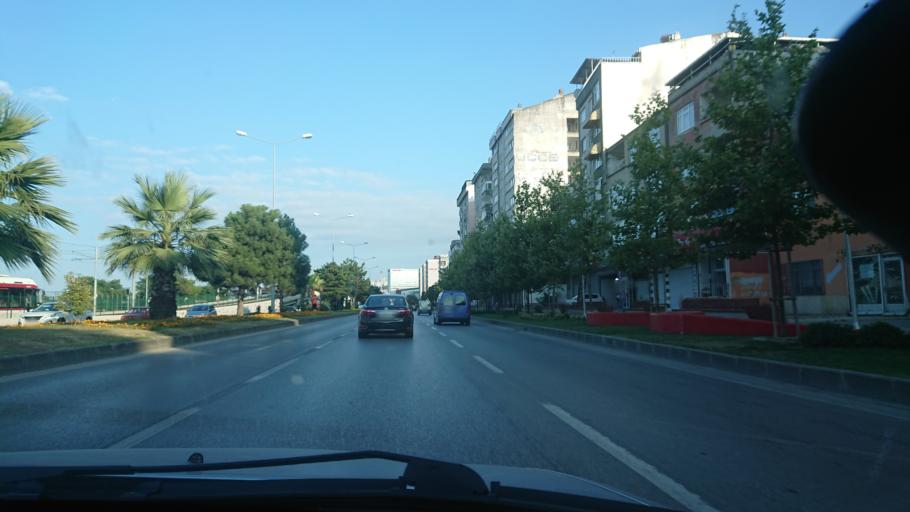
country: TR
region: Samsun
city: Samsun
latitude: 41.2824
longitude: 36.3461
